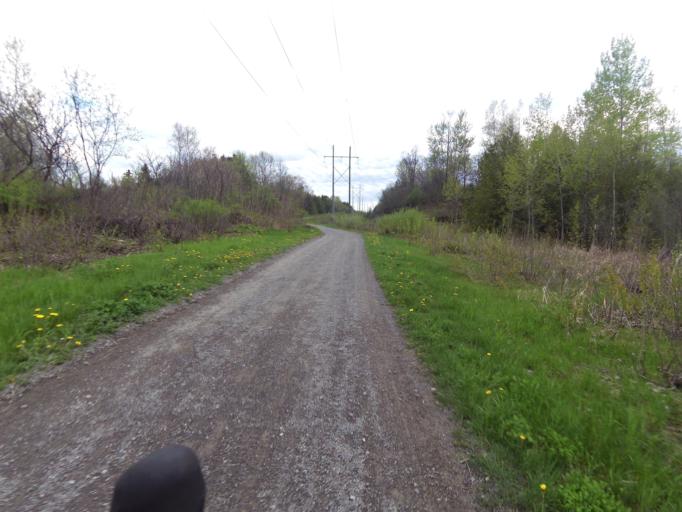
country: CA
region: Ontario
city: Bells Corners
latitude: 45.2847
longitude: -75.8018
